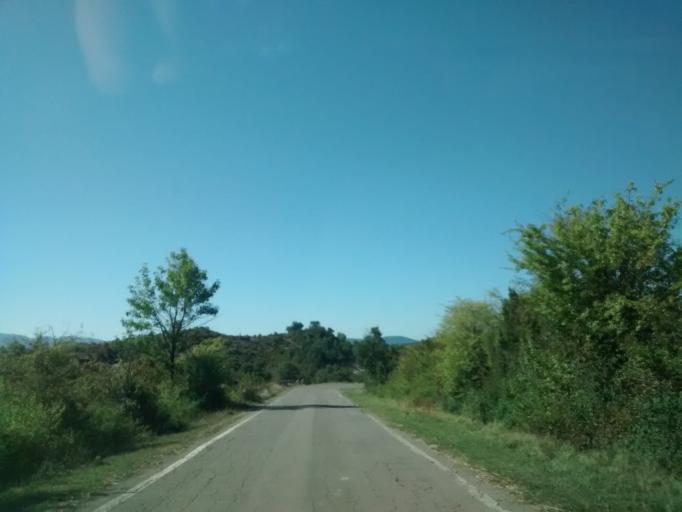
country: ES
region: Aragon
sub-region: Provincia de Huesca
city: Santa Cruz de la Seros
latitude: 42.4780
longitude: -0.5893
